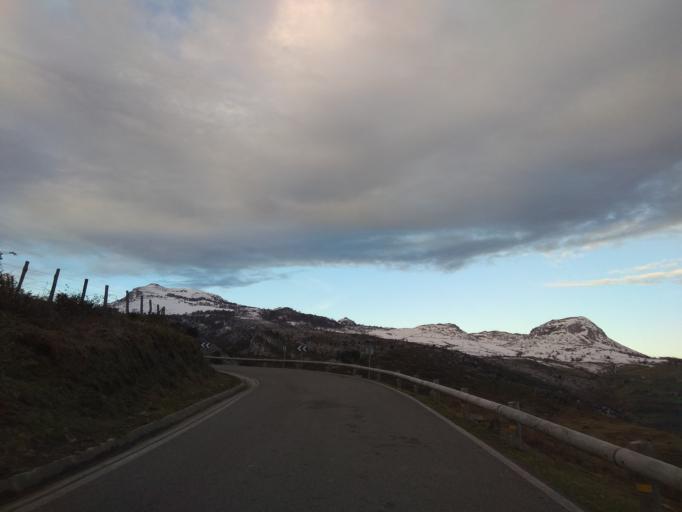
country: ES
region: Cantabria
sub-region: Provincia de Cantabria
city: Arredondo
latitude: 43.1980
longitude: -3.5825
